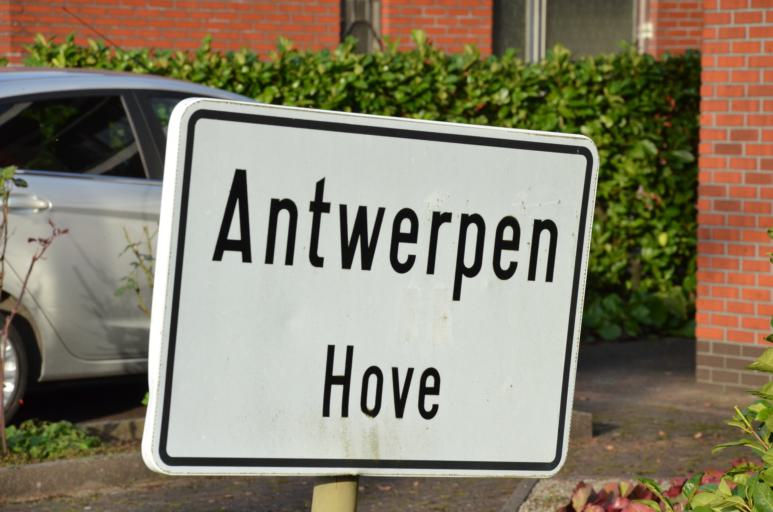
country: BE
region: Flanders
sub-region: Provincie Antwerpen
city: Hove
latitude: 51.1418
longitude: 4.4725
